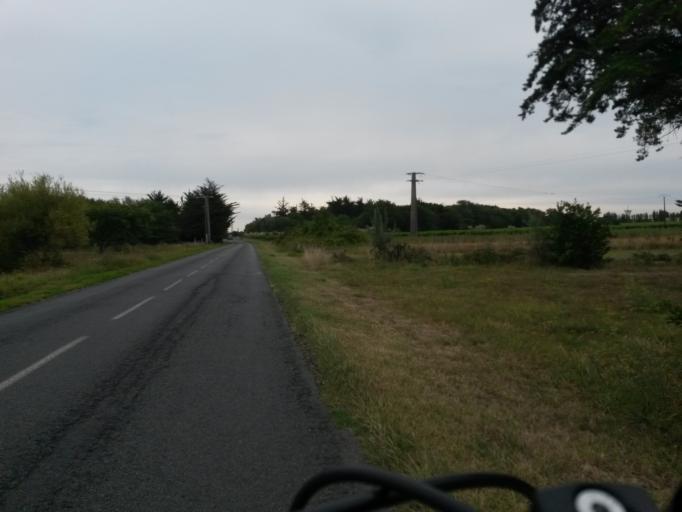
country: FR
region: Poitou-Charentes
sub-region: Departement de la Charente-Maritime
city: Dolus-d'Oleron
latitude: 45.9407
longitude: -1.3347
